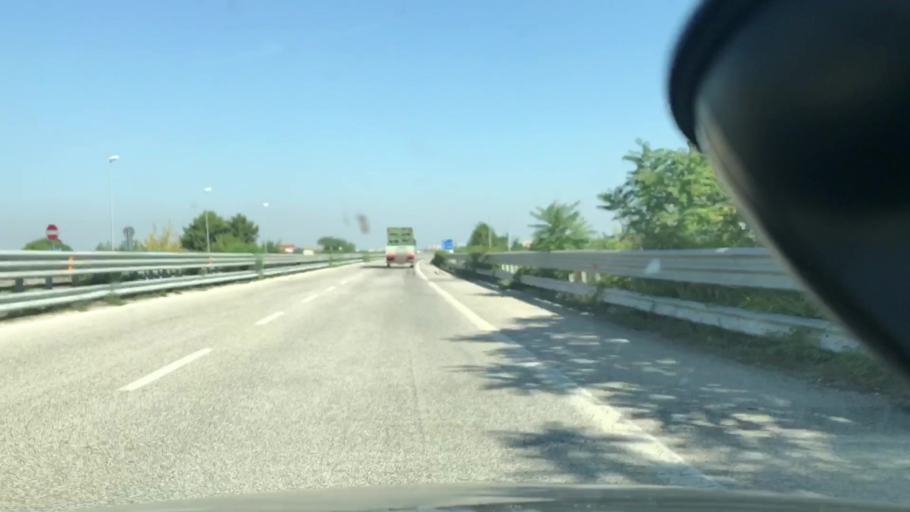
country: IT
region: Apulia
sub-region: Provincia di Foggia
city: Foggia
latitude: 41.4150
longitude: 15.5585
